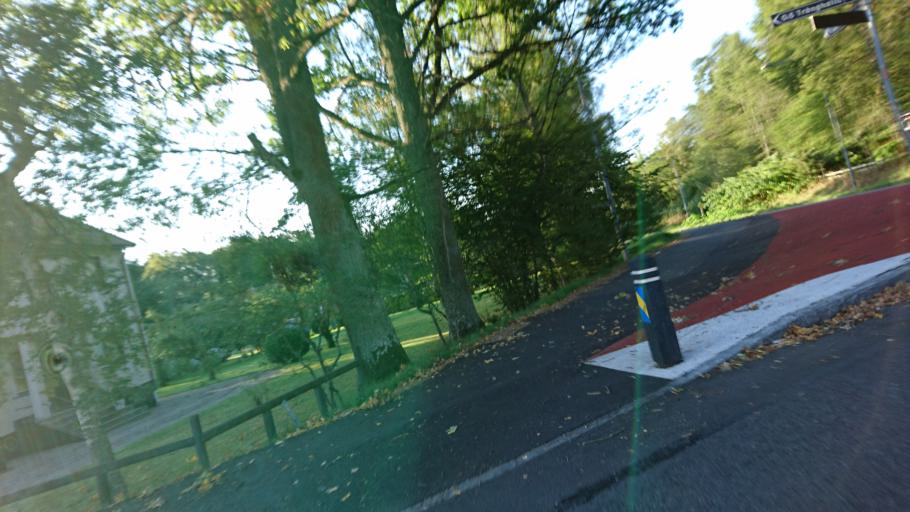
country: SE
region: Joenkoeping
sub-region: Jonkopings Kommun
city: Bankeryd
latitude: 57.8336
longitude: 14.1432
